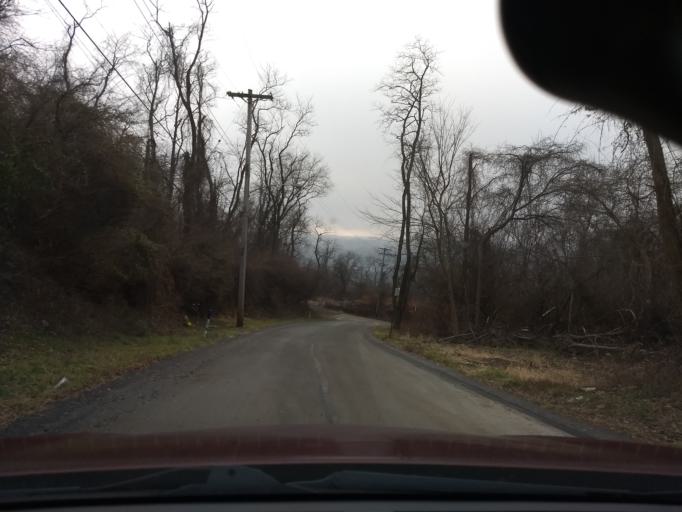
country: US
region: Pennsylvania
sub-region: Allegheny County
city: East Pittsburgh
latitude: 40.3867
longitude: -79.8440
